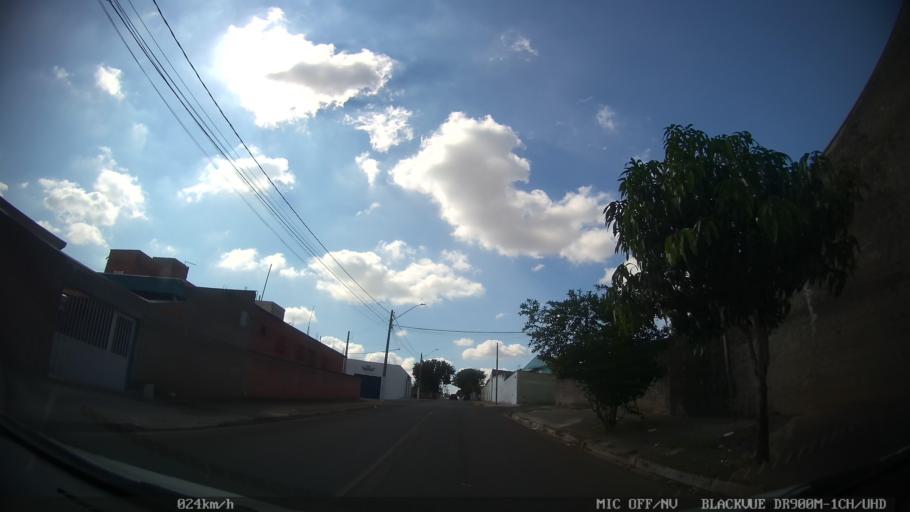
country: BR
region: Sao Paulo
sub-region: Hortolandia
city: Hortolandia
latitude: -22.8825
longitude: -47.2102
